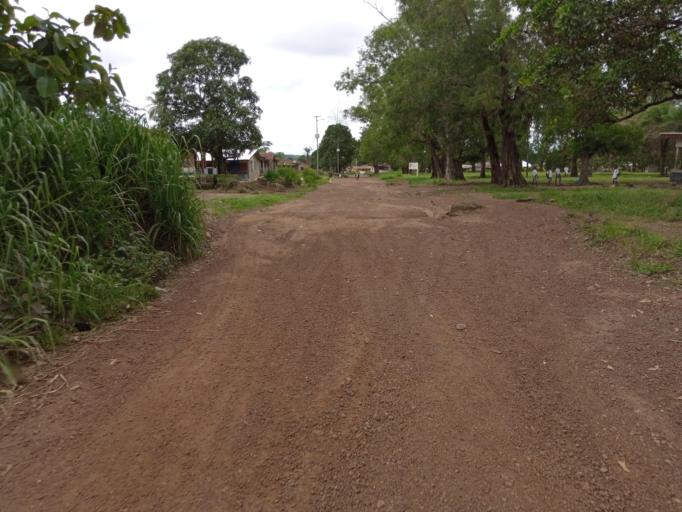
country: SL
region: Southern Province
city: Moyamba
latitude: 8.1657
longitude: -12.4243
